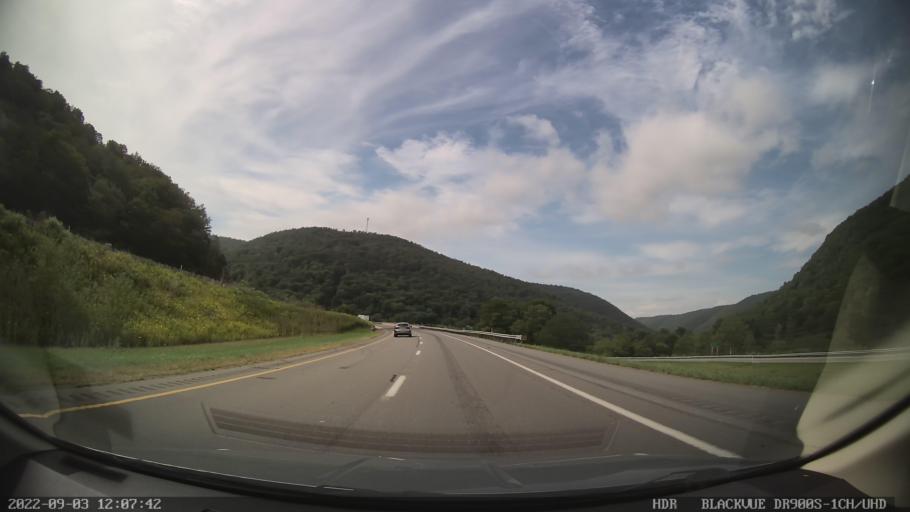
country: US
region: Pennsylvania
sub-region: Tioga County
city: Blossburg
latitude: 41.4955
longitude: -77.1465
